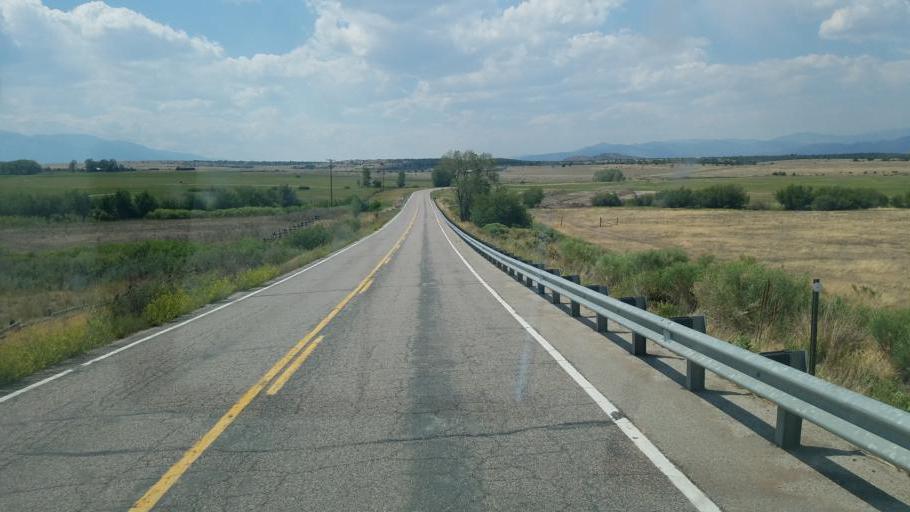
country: US
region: Colorado
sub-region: Custer County
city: Westcliffe
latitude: 38.2871
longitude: -105.6171
